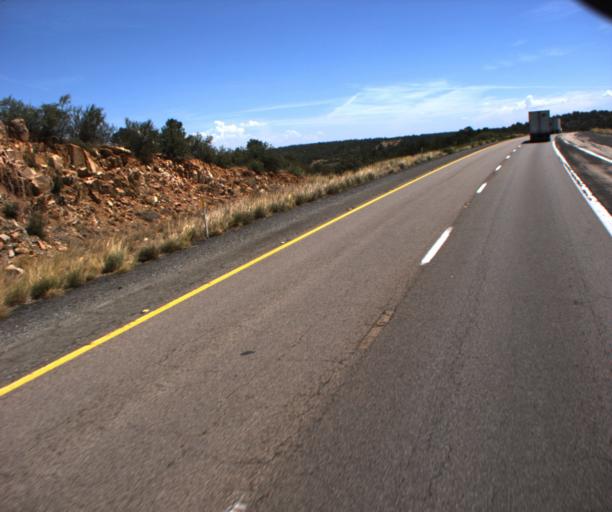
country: US
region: Arizona
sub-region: Mohave County
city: Peach Springs
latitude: 35.2071
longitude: -113.2916
